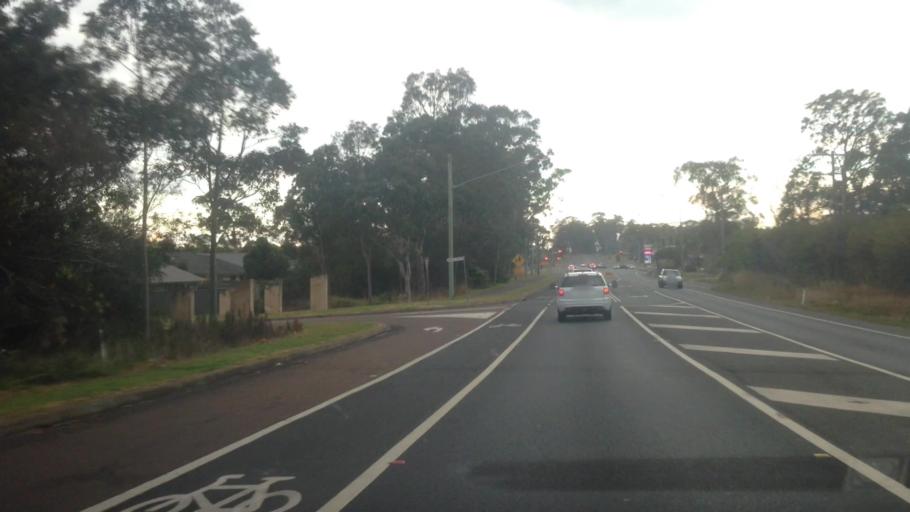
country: AU
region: New South Wales
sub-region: Wyong Shire
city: Tuggerawong
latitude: -33.2622
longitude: 151.4609
